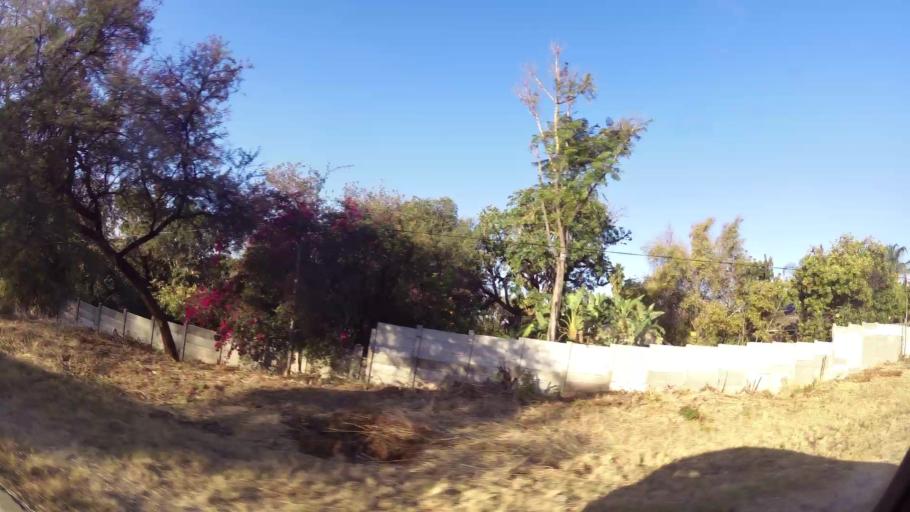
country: ZA
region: North-West
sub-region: Bojanala Platinum District Municipality
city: Rustenburg
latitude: -25.6987
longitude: 27.2187
